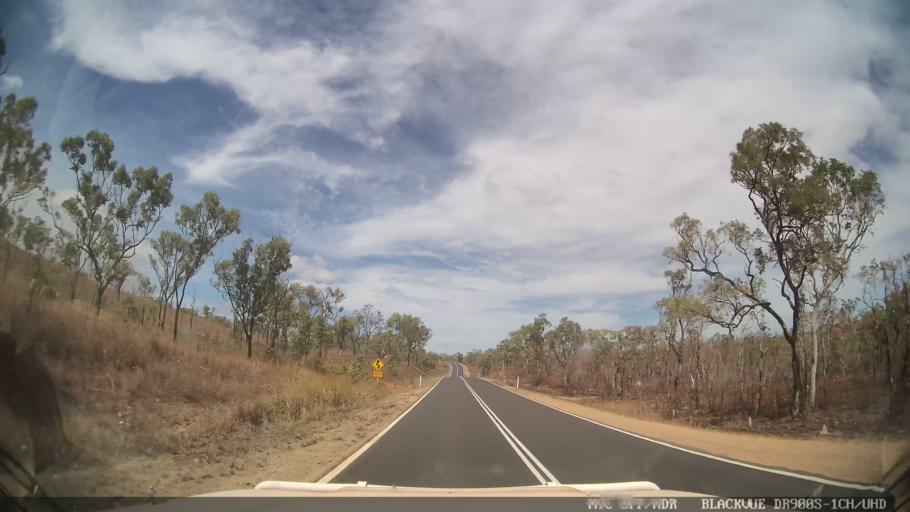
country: AU
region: Queensland
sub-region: Cairns
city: Port Douglas
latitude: -16.6680
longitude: 145.2594
